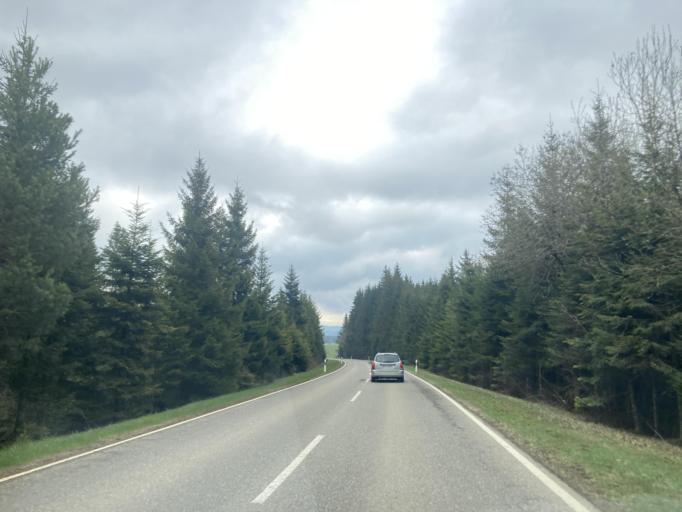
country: DE
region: Baden-Wuerttemberg
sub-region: Freiburg Region
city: Unterkirnach
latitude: 48.0266
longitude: 8.3646
